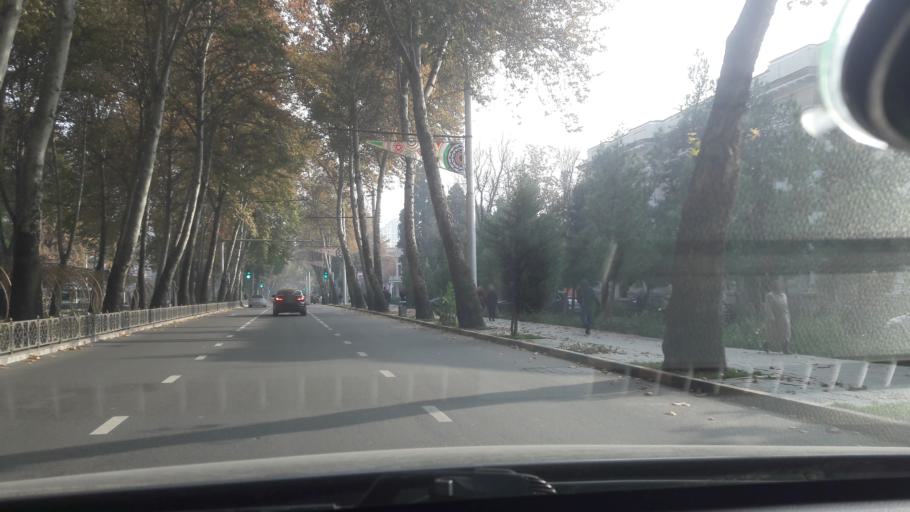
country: TJ
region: Dushanbe
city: Dushanbe
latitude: 38.5688
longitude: 68.7919
